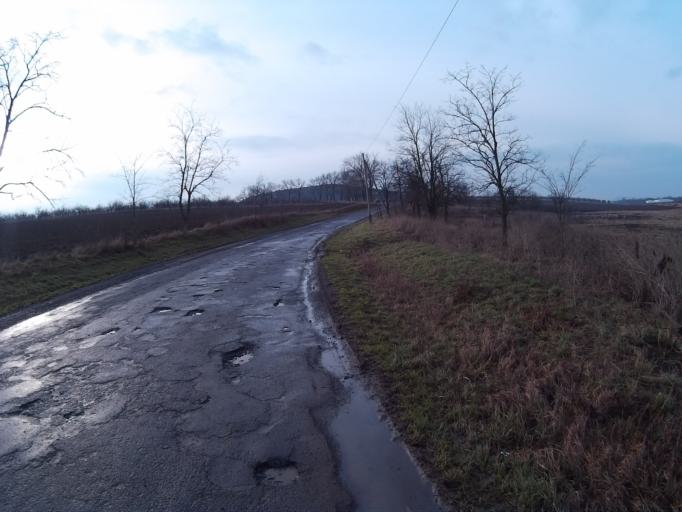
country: HU
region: Borsod-Abauj-Zemplen
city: Abaujszanto
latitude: 48.3450
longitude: 21.2145
